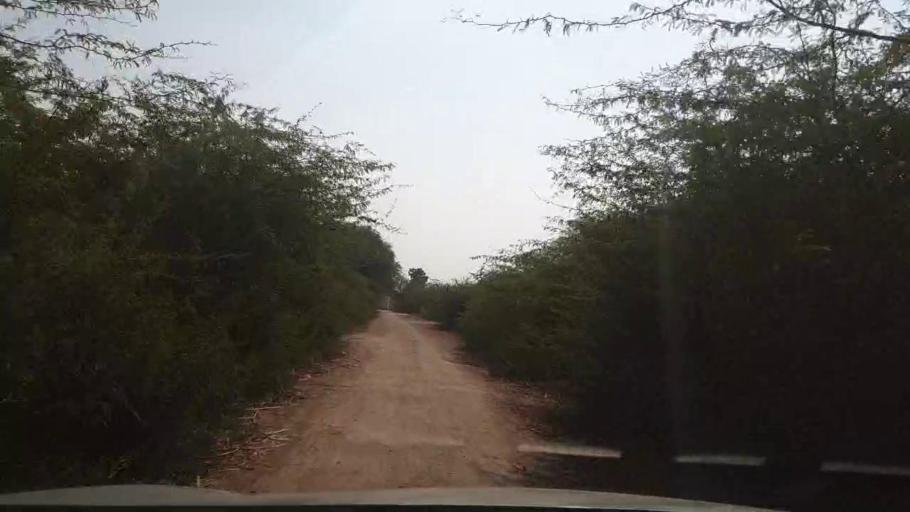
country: PK
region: Sindh
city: Tando Allahyar
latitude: 25.5555
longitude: 68.8477
